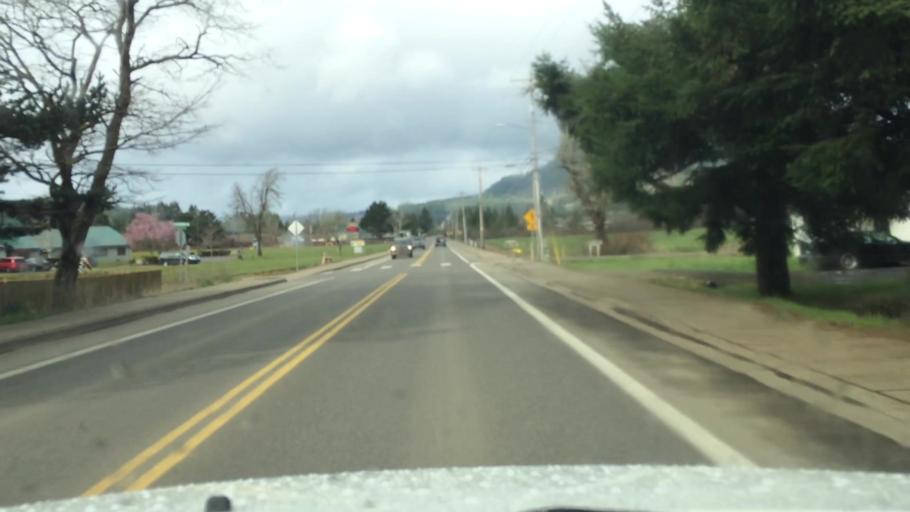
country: US
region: Oregon
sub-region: Polk County
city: Grand Ronde
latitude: 45.0722
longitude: -123.6118
